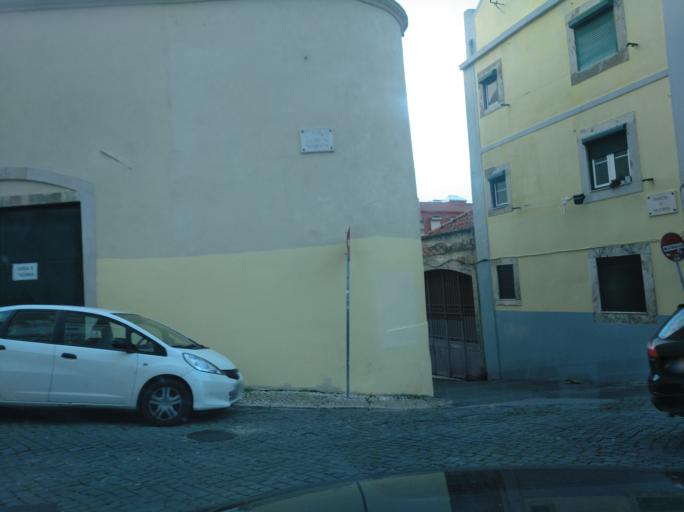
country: PT
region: Lisbon
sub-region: Lisbon
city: Lisbon
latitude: 38.7212
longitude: -9.1334
